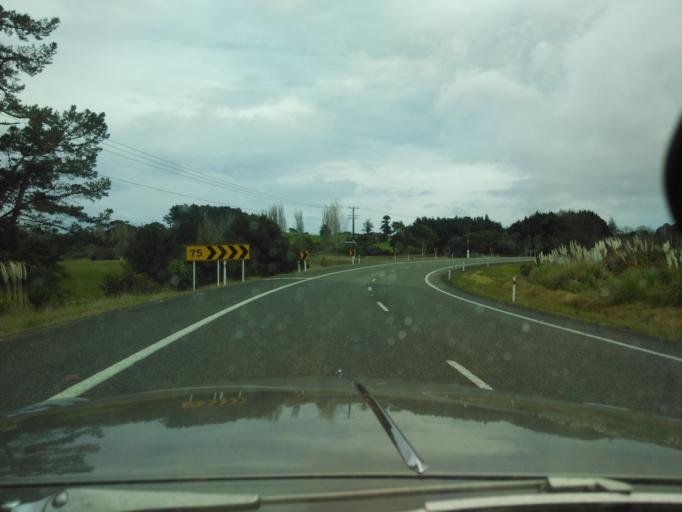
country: NZ
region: Auckland
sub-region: Auckland
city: Muriwai Beach
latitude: -36.7569
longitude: 174.4512
